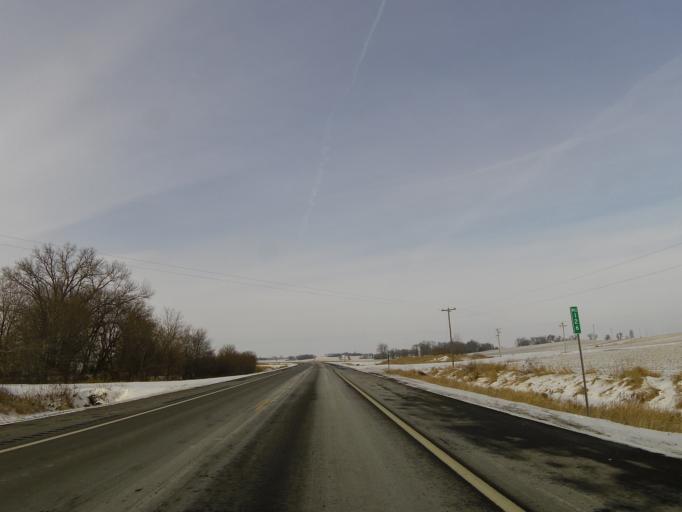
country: US
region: Minnesota
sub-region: McLeod County
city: Hutchinson
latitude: 44.9052
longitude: -94.4400
